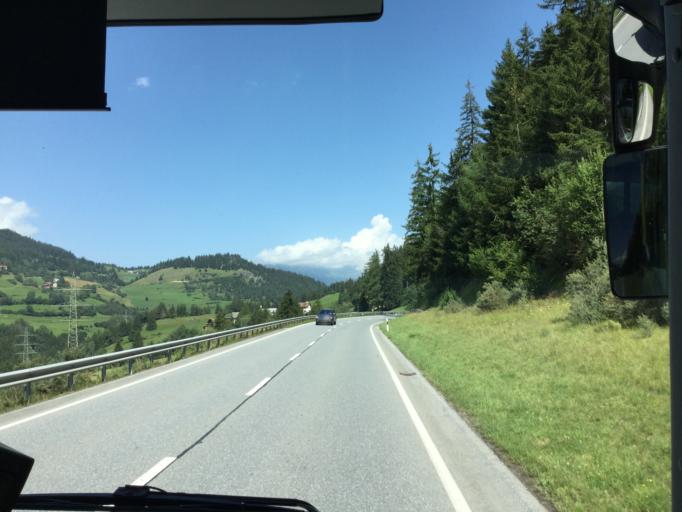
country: CH
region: Grisons
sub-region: Albula District
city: Tiefencastel
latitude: 46.6206
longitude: 9.5902
